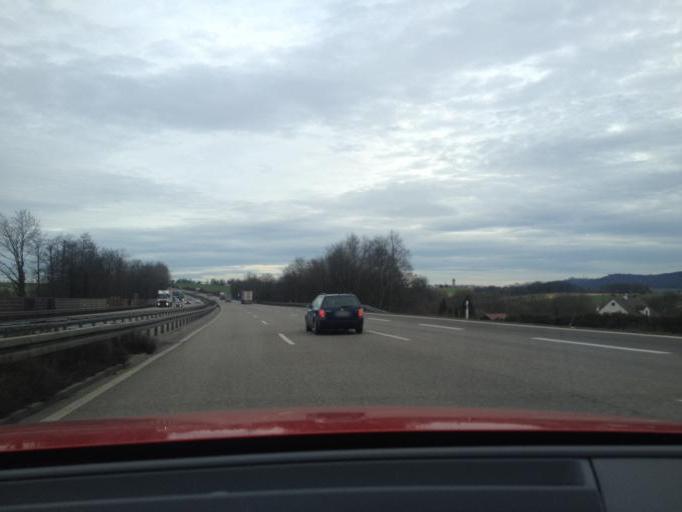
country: DE
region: Baden-Wuerttemberg
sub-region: Regierungsbezirk Stuttgart
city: Ohringen
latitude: 49.2119
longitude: 9.5383
